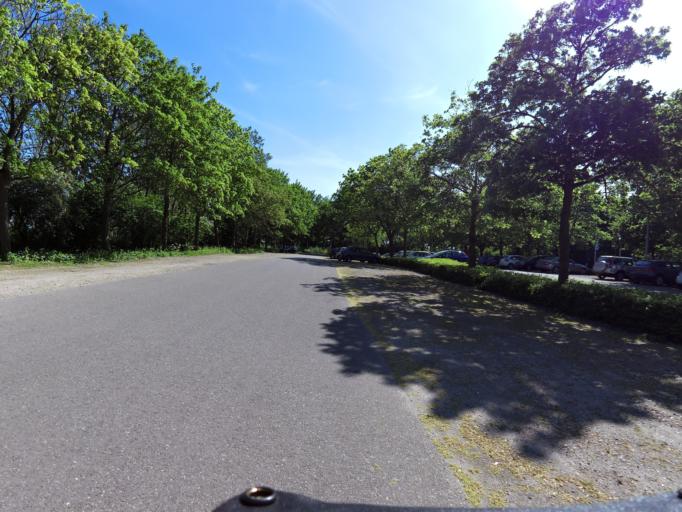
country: NL
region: South Holland
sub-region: Gemeente Barendrecht
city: Barendrecht
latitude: 51.8343
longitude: 4.5262
